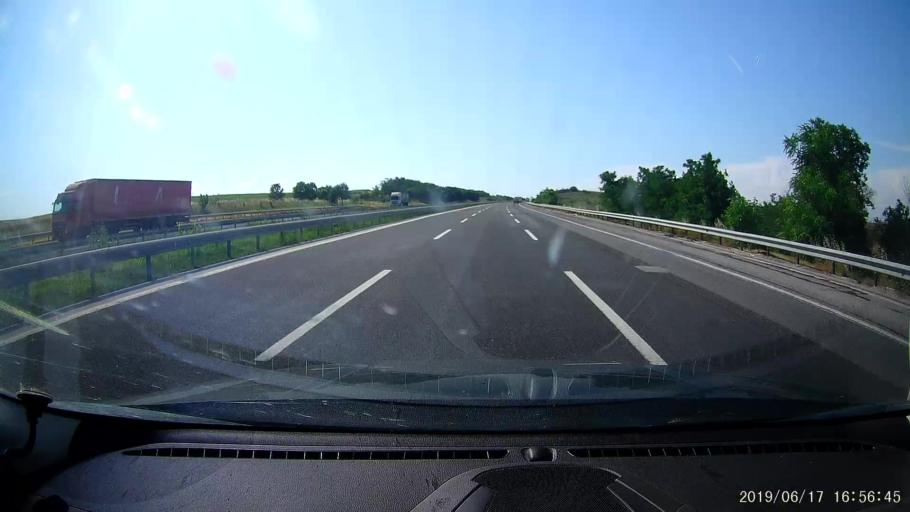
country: TR
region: Edirne
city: Haskoy
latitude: 41.5902
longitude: 26.9294
